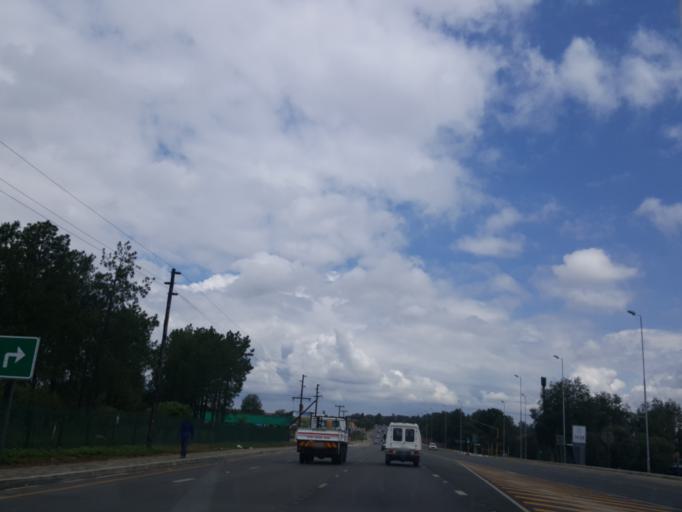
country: ZA
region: Gauteng
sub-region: City of Johannesburg Metropolitan Municipality
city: Diepsloot
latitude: -26.0019
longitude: 27.9860
